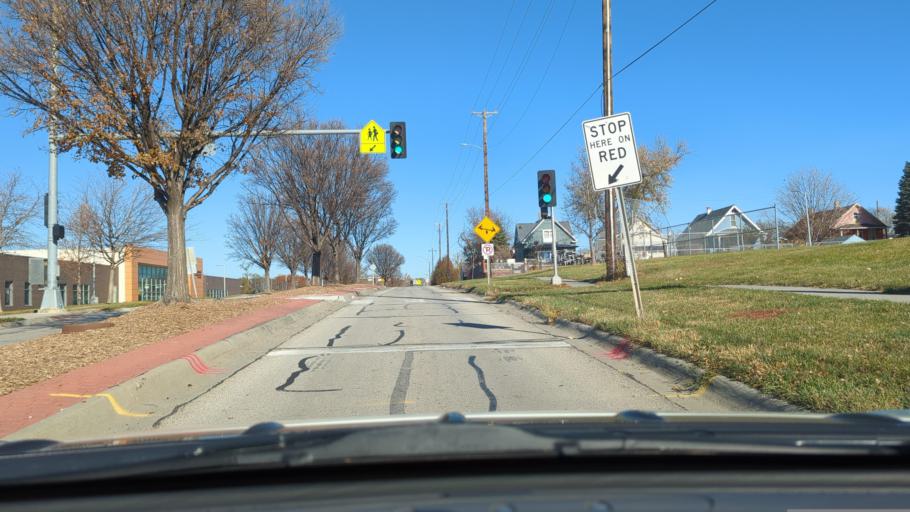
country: US
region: Nebraska
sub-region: Sarpy County
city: La Vista
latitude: 41.2002
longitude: -95.9770
